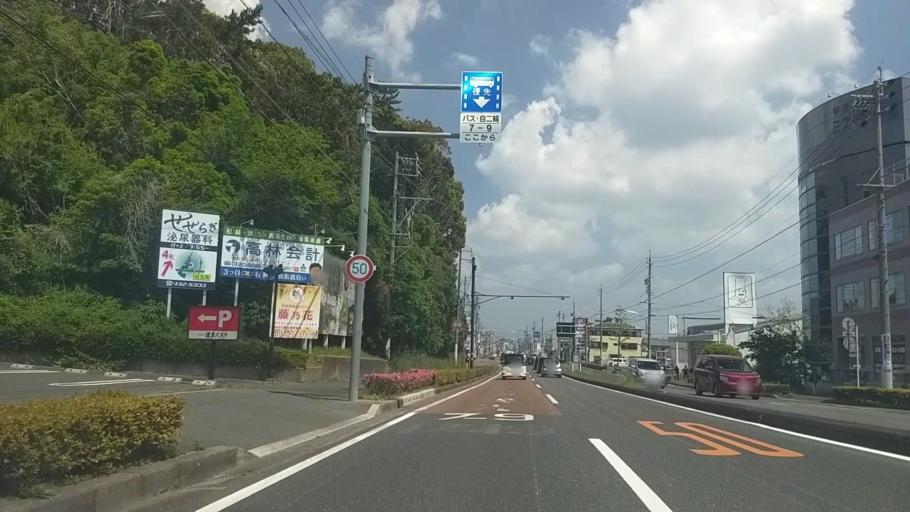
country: JP
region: Shizuoka
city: Hamamatsu
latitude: 34.7236
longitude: 137.7306
